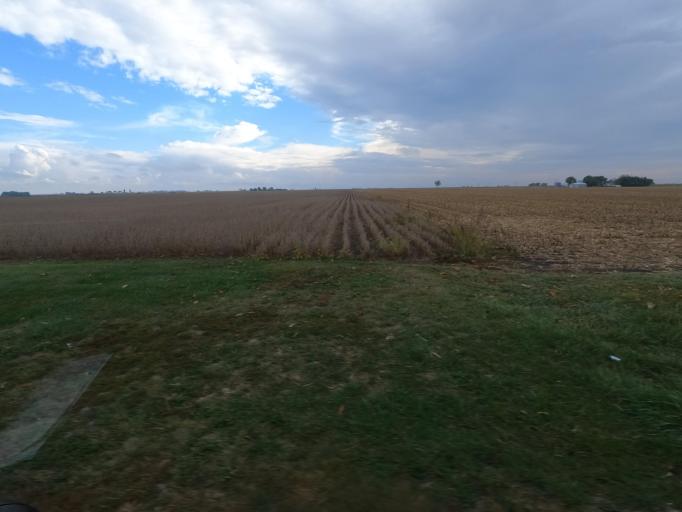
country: US
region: Iowa
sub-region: Henry County
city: Mount Pleasant
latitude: 40.7846
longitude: -91.6363
